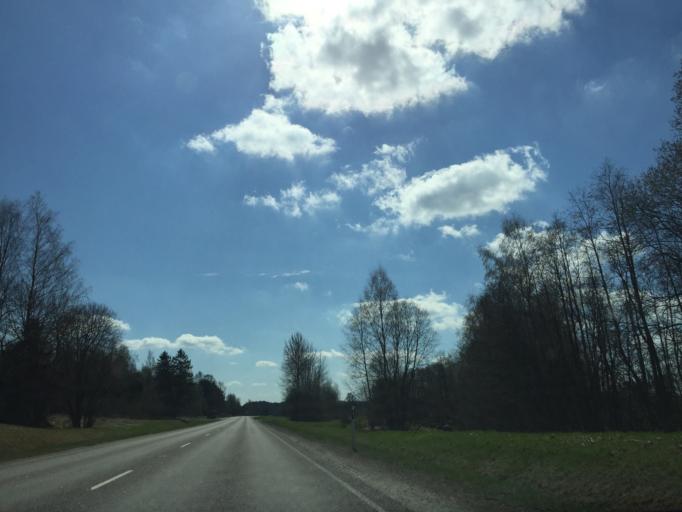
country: EE
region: Tartu
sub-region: Elva linn
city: Elva
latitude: 58.0957
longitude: 26.2281
